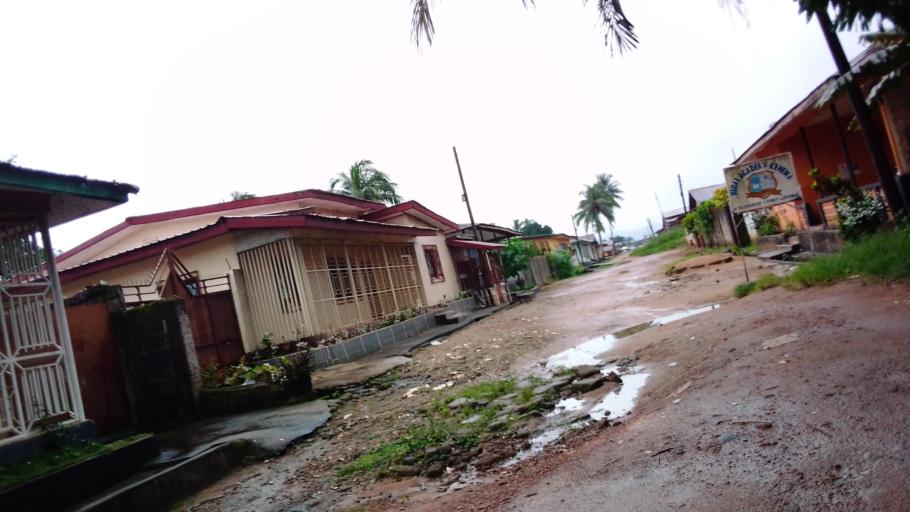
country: SL
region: Eastern Province
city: Kenema
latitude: 7.8864
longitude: -11.1899
